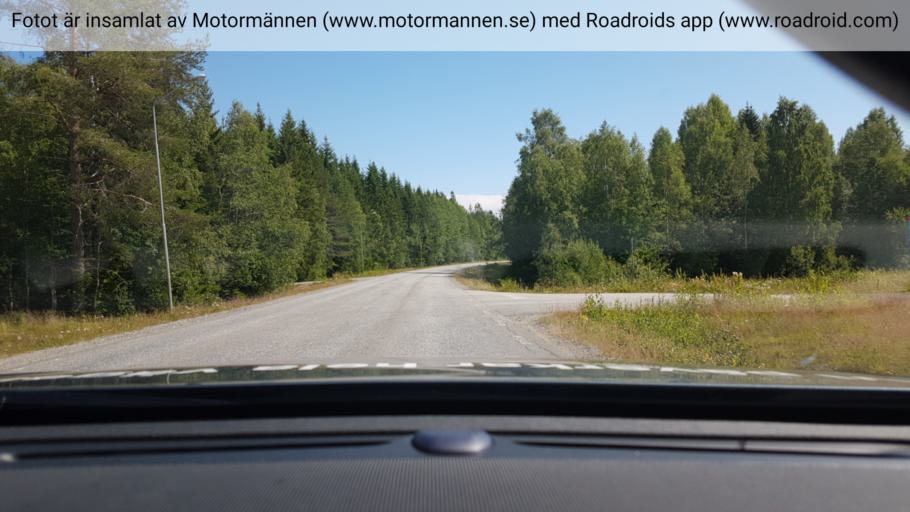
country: SE
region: Vaesterbotten
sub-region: Robertsfors Kommun
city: Robertsfors
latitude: 64.2017
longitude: 20.8276
